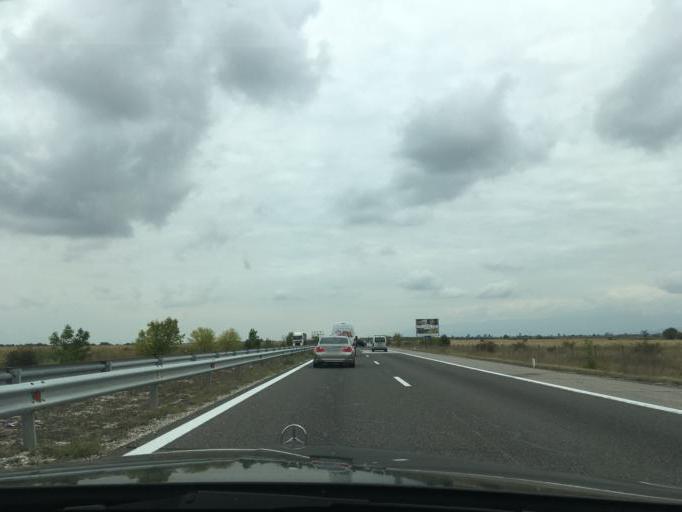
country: BG
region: Pazardzhik
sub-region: Obshtina Pazardzhik
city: Pazardzhik
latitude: 42.2501
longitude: 24.3449
